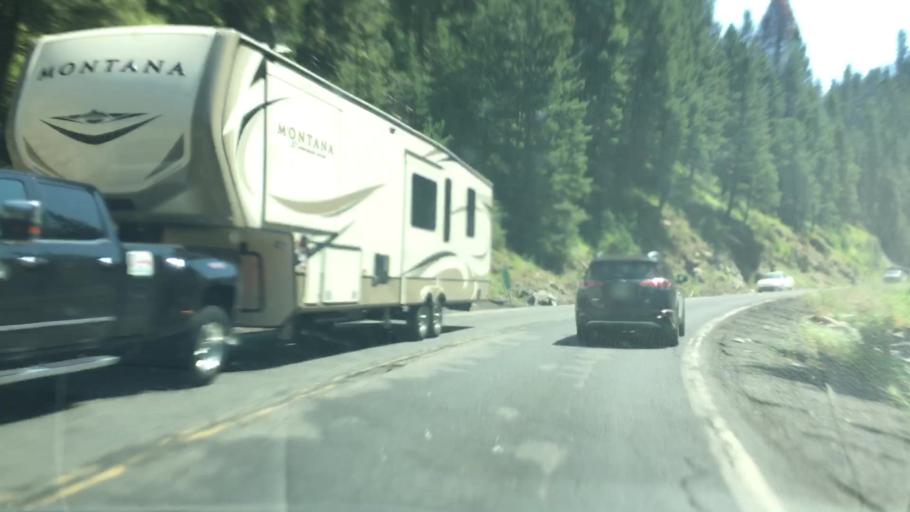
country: US
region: Idaho
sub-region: Valley County
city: McCall
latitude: 44.9632
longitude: -116.1738
